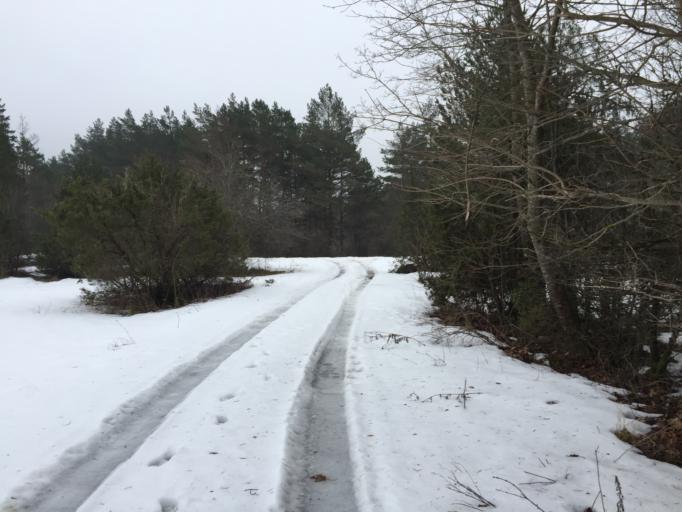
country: EE
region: Saare
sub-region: Orissaare vald
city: Orissaare
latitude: 58.4166
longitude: 22.8235
